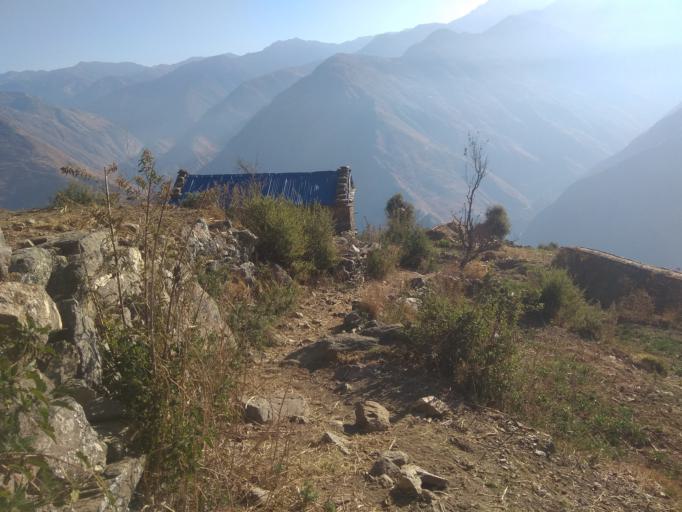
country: NP
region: Mid Western
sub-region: Karnali Zone
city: Jumla
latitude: 29.3138
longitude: 81.7390
